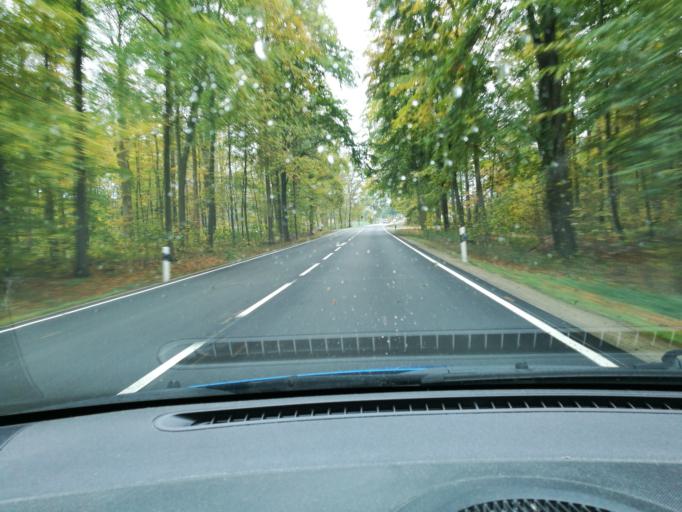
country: DE
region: Schleswig-Holstein
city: Fredeburg
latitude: 53.6552
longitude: 10.7125
